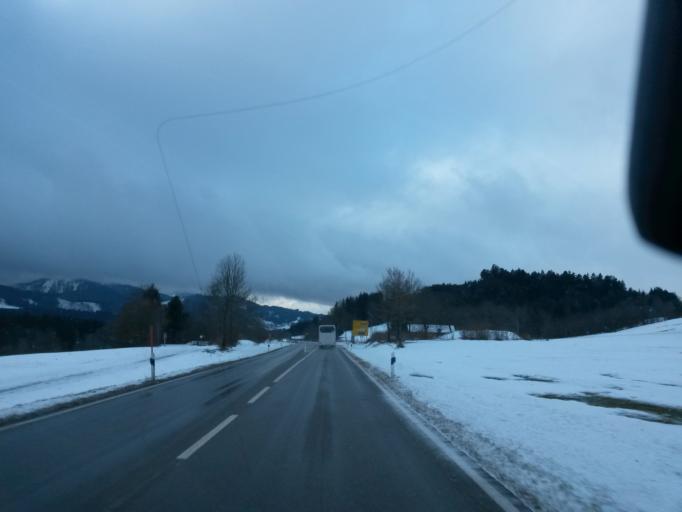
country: DE
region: Bavaria
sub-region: Swabia
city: Oy-Mittelberg
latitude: 47.6230
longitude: 10.4430
